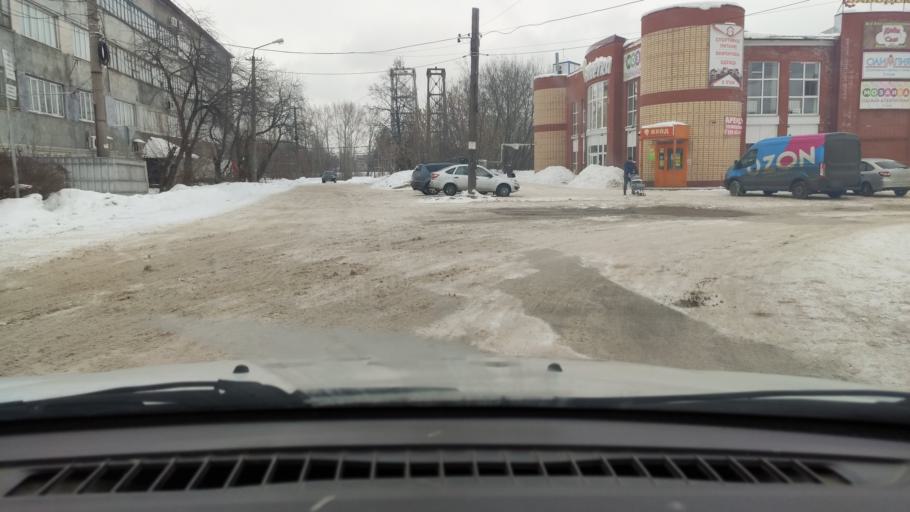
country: RU
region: Perm
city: Kungur
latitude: 57.4416
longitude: 56.9312
